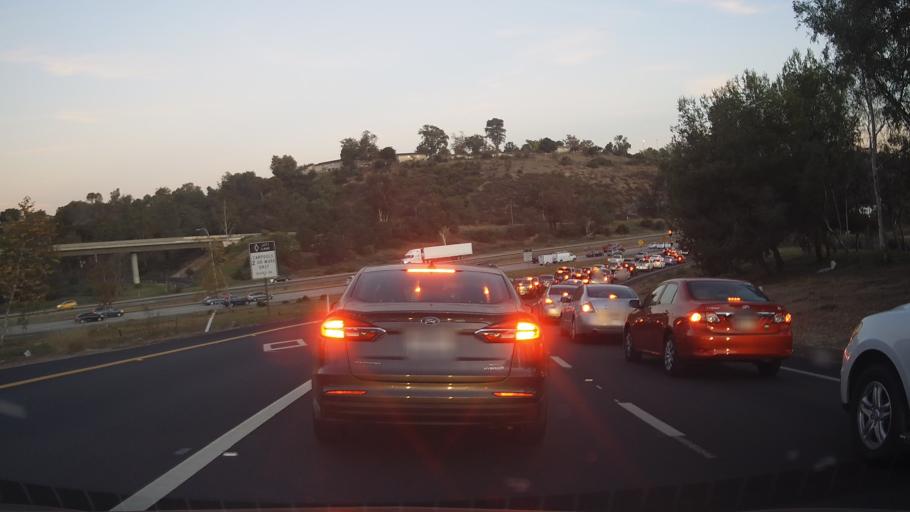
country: US
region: California
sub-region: San Diego County
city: La Mesa
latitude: 32.8221
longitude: -117.1178
